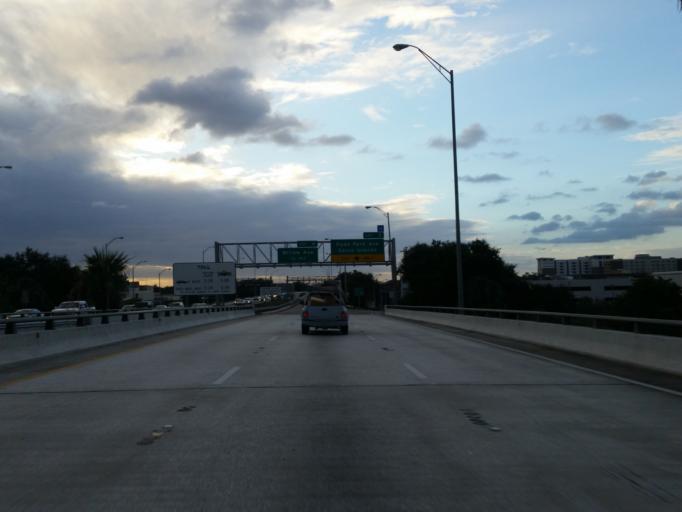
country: US
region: Florida
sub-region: Hillsborough County
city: Tampa
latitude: 27.9432
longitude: -82.4593
